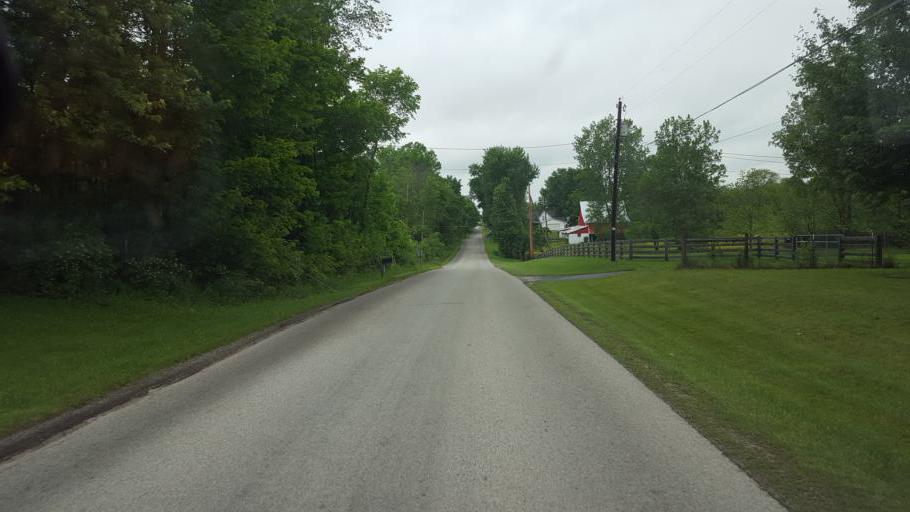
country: US
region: Ohio
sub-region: Morrow County
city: Mount Gilead
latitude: 40.4615
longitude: -82.7922
